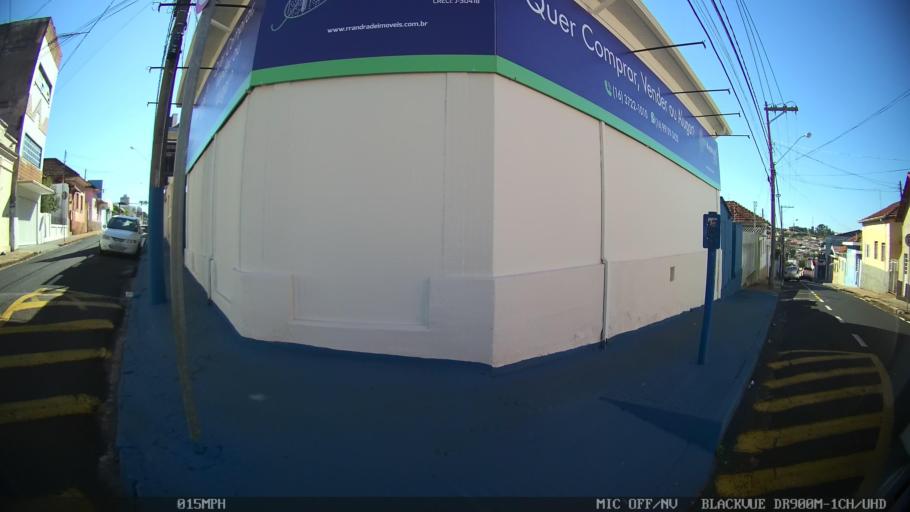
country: BR
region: Sao Paulo
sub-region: Franca
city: Franca
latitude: -20.5427
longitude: -47.3997
